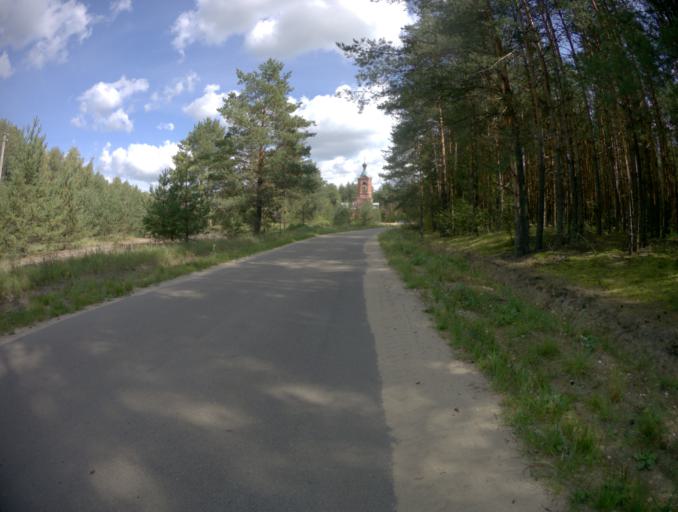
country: RU
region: Vladimir
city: Pokrov
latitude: 55.8644
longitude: 39.3053
